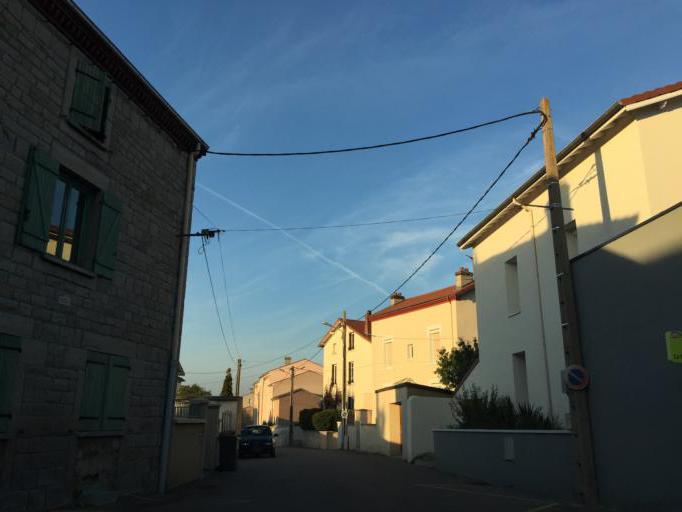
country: FR
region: Rhone-Alpes
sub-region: Departement de la Loire
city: Saint-Chamond
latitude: 45.4628
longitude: 4.5004
